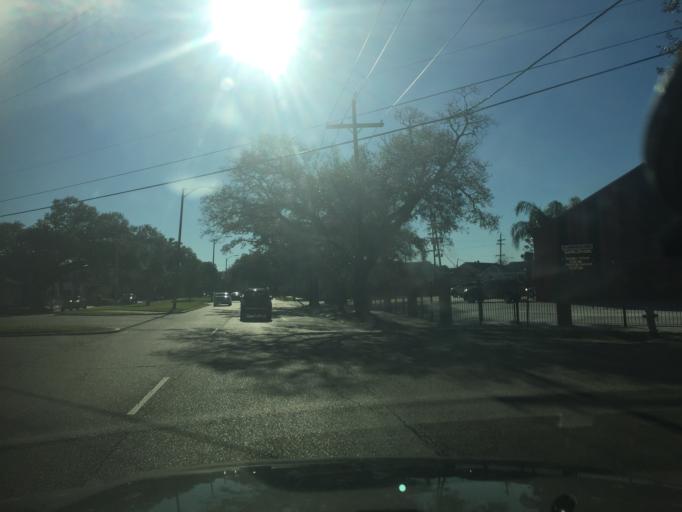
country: US
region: Louisiana
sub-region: Orleans Parish
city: New Orleans
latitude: 29.9866
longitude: -90.0689
